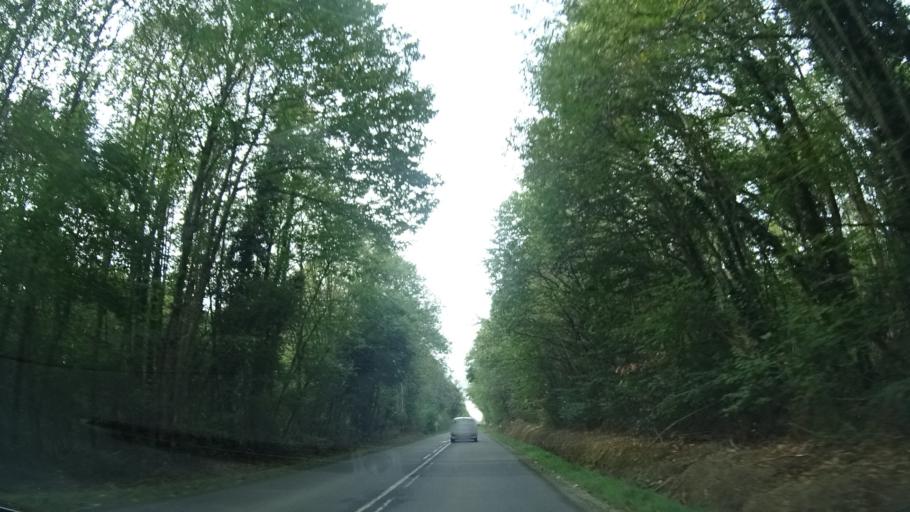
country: FR
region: Brittany
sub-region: Departement d'Ille-et-Vilaine
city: Meillac
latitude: 48.4303
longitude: -1.7859
